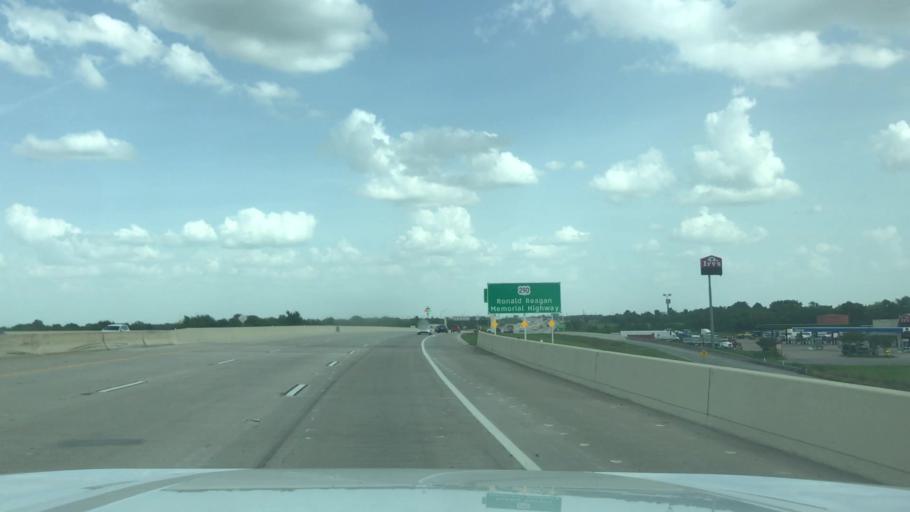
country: US
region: Texas
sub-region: Waller County
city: Waller
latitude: 30.0687
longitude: -95.9216
